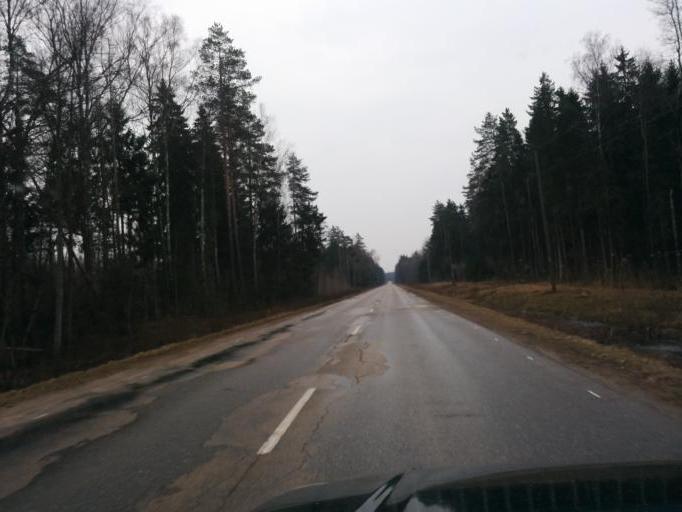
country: LV
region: Ikskile
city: Ikskile
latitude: 56.8129
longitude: 24.4782
